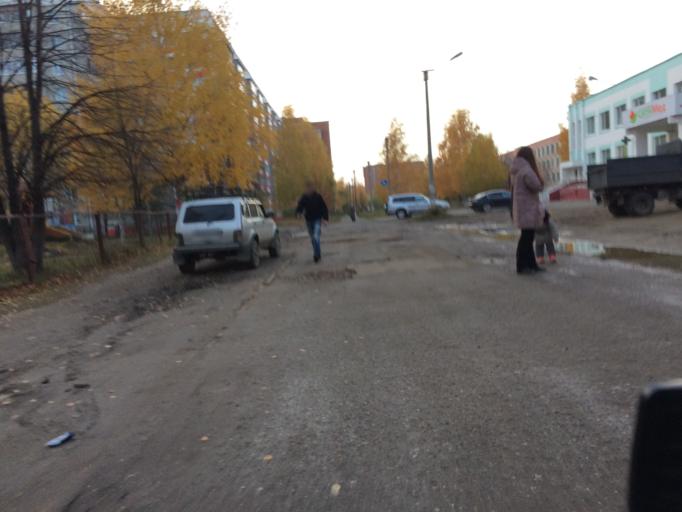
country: RU
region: Mariy-El
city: Yoshkar-Ola
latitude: 56.6318
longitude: 47.9254
